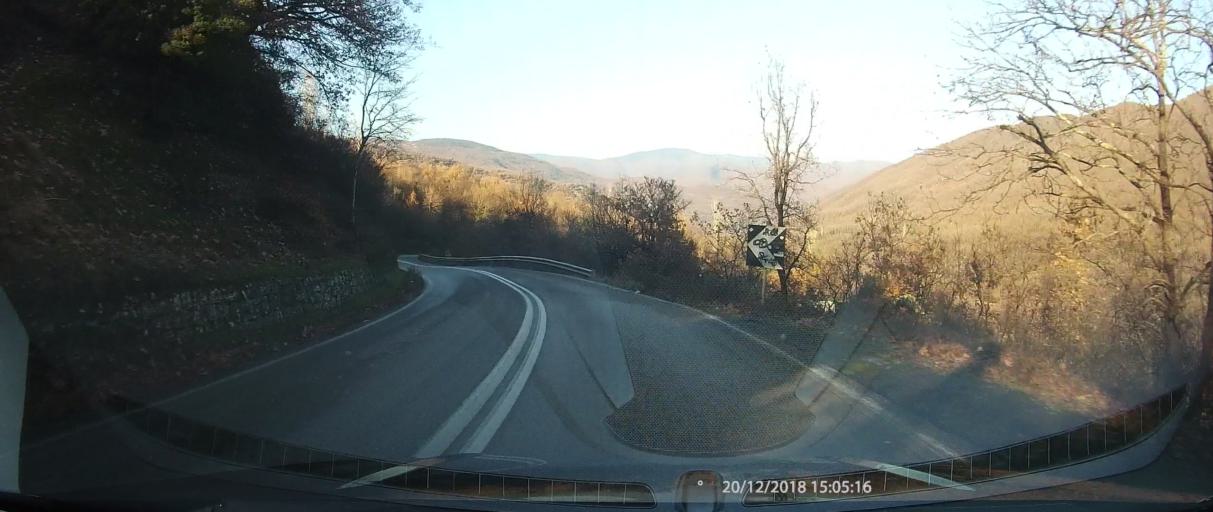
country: GR
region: Central Greece
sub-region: Nomos Evrytanias
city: Karpenisi
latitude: 38.9099
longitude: 21.9284
